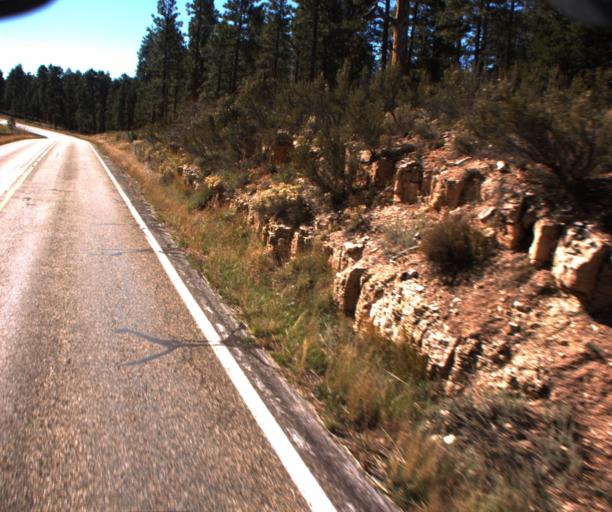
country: US
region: Arizona
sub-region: Coconino County
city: Fredonia
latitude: 36.7534
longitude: -112.2693
